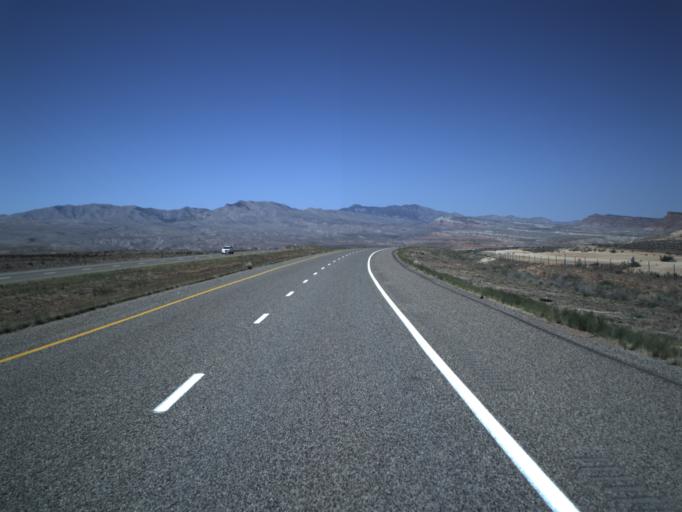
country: US
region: Utah
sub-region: Washington County
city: Saint George
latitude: 37.0036
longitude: -113.5816
